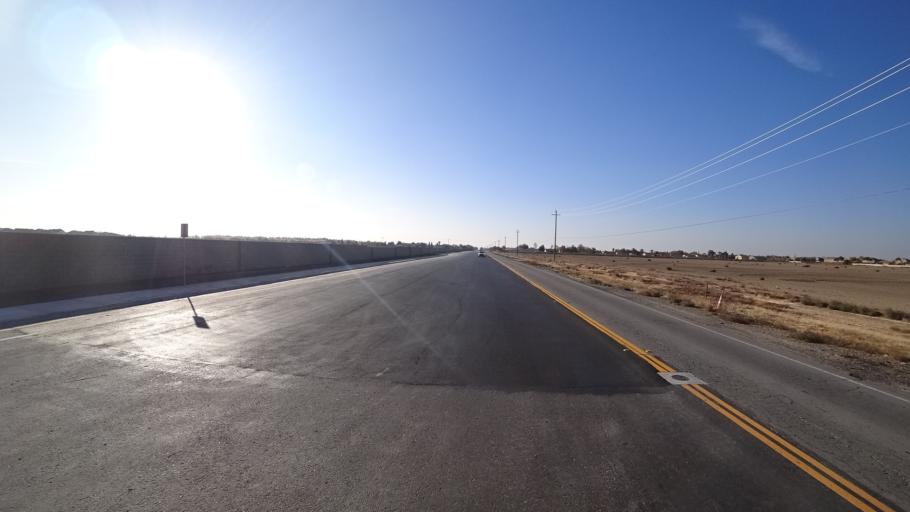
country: US
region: California
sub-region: Kern County
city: Greenacres
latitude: 35.2961
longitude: -119.1143
